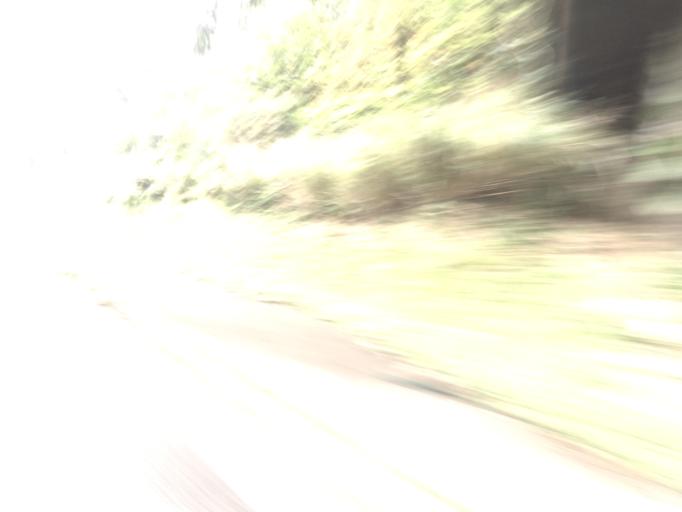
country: US
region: Hawaii
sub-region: Honolulu County
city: Kane'ohe
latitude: 21.3758
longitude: -157.8191
